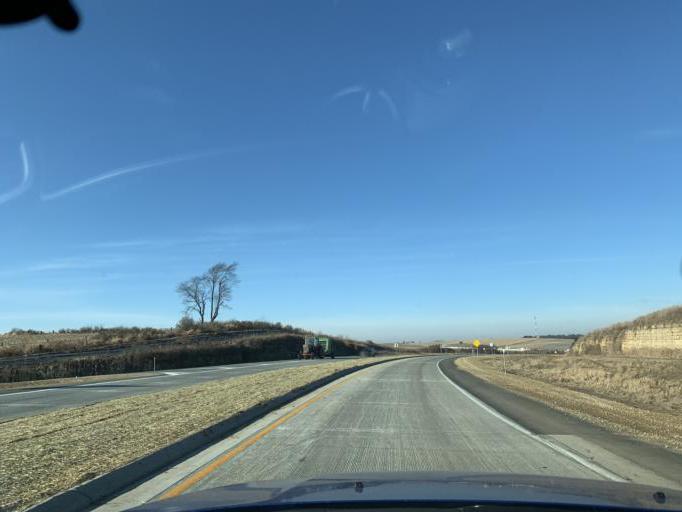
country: US
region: Wisconsin
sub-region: Iowa County
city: Dodgeville
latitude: 42.9380
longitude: -90.1320
